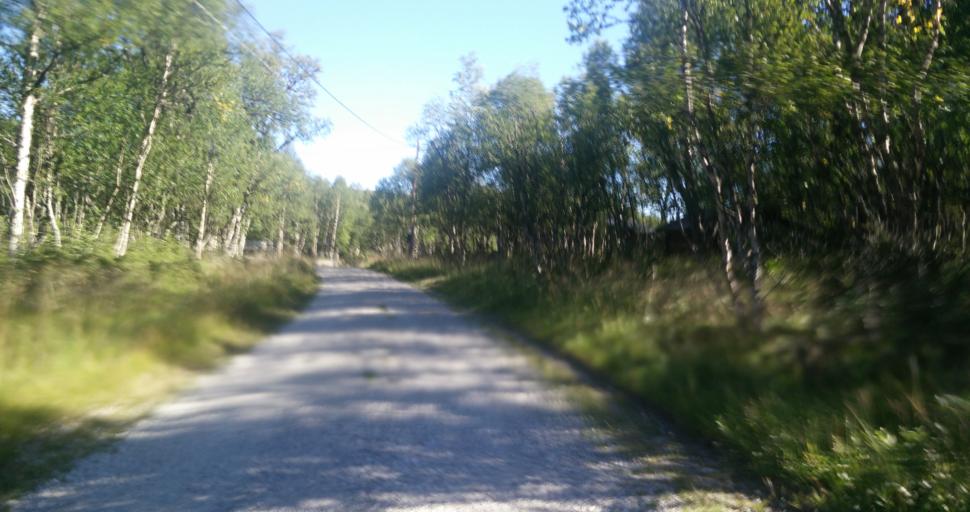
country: NO
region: Sor-Trondelag
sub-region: Tydal
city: Aas
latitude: 62.6957
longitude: 12.3990
